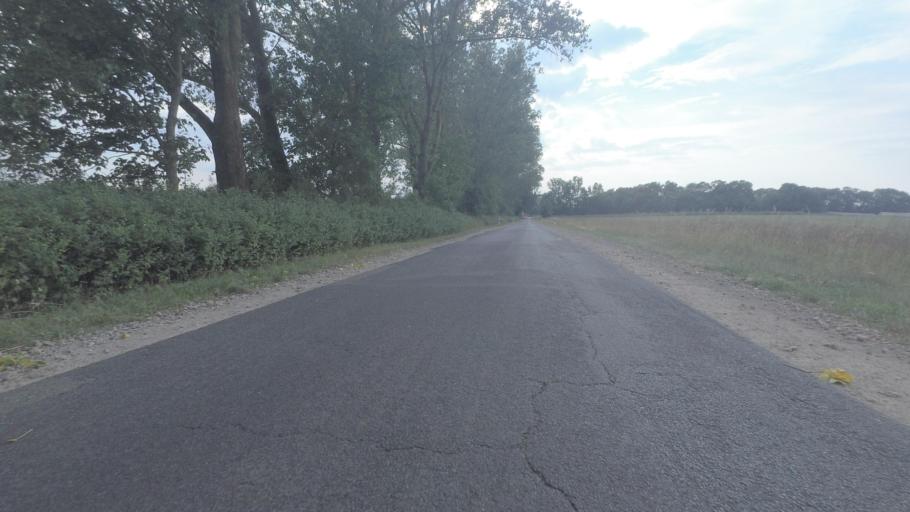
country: DE
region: Brandenburg
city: Heiligengrabe
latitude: 53.2431
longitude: 12.3699
